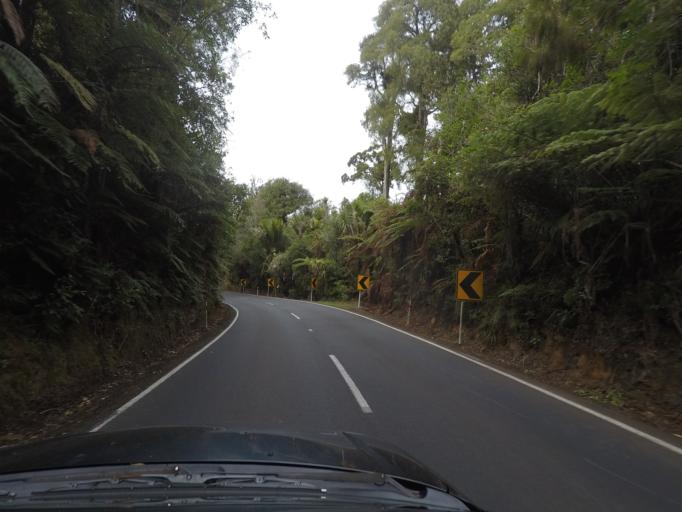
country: NZ
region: Auckland
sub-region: Auckland
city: Titirangi
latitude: -36.9425
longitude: 174.5908
